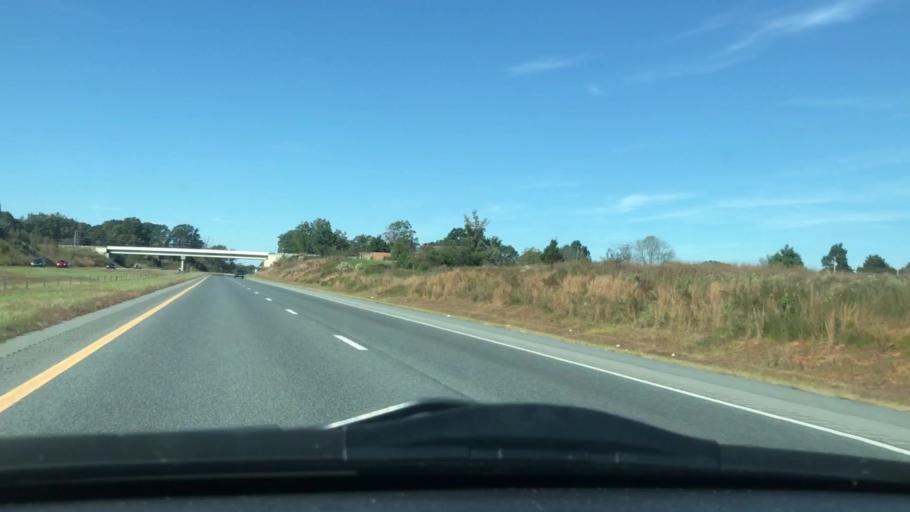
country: US
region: North Carolina
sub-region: Randolph County
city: Randleman
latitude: 35.8536
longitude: -79.8789
